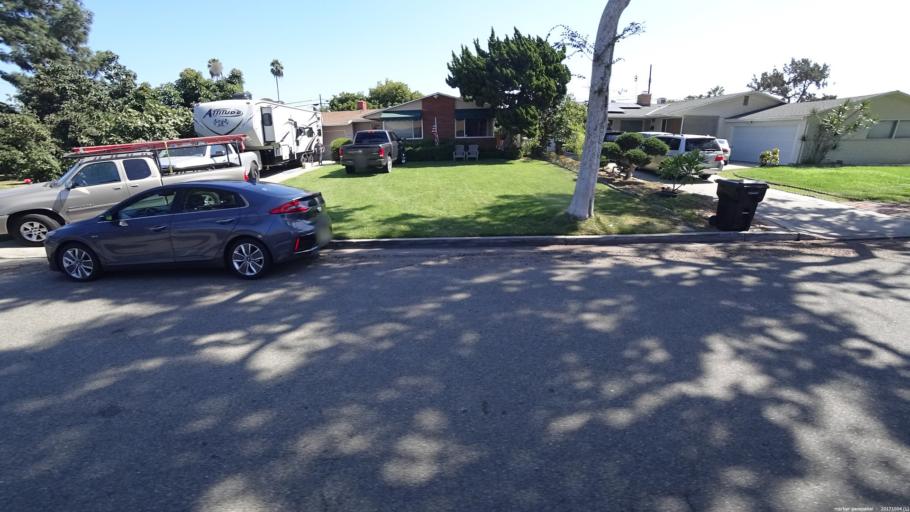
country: US
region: California
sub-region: Orange County
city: Garden Grove
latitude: 33.7912
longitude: -117.9549
